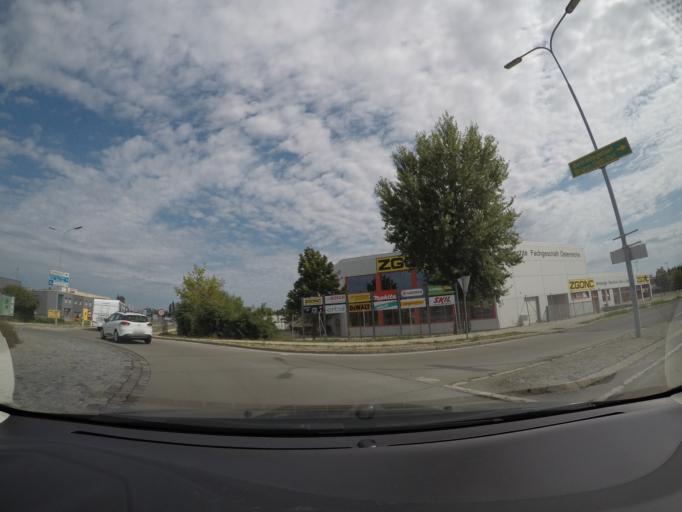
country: AT
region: Lower Austria
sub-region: Politischer Bezirk Modling
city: Brunn am Gebirge
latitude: 48.1095
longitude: 16.3060
